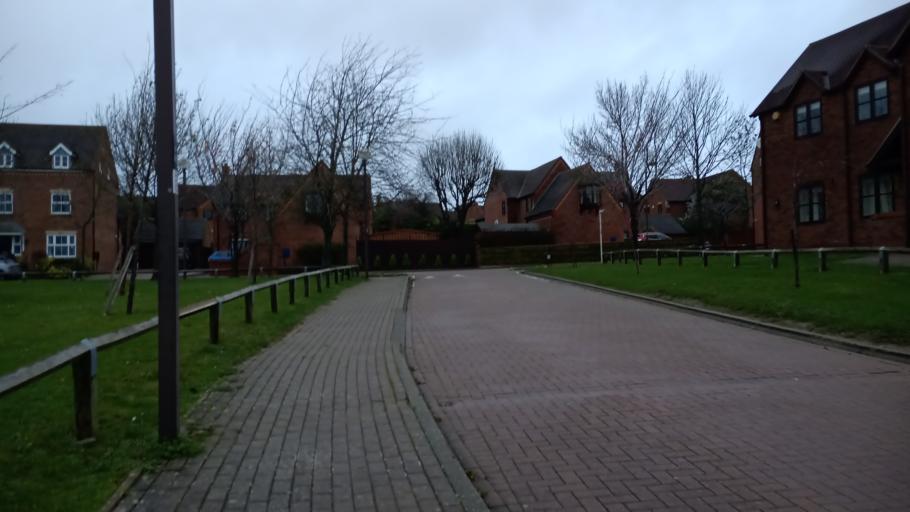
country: GB
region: England
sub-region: Milton Keynes
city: Shenley Church End
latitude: 52.0117
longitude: -0.7897
